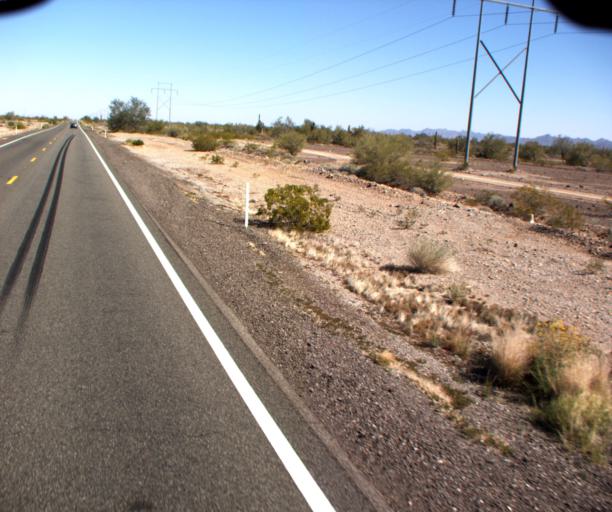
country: US
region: Arizona
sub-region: La Paz County
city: Quartzsite
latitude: 33.5461
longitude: -114.2170
